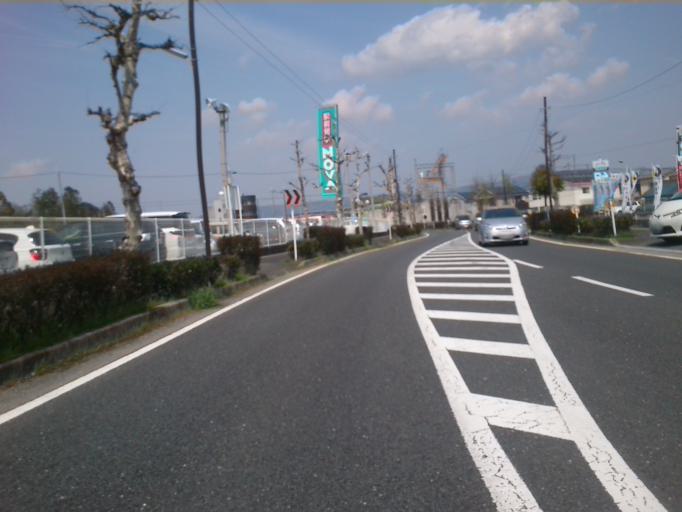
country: JP
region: Nara
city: Nara-shi
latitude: 34.7383
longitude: 135.7932
